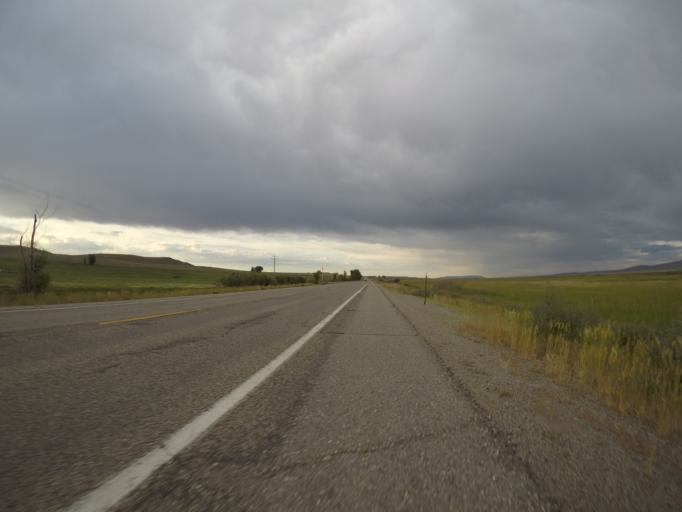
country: US
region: Utah
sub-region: Rich County
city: Randolph
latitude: 42.0087
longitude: -110.9373
